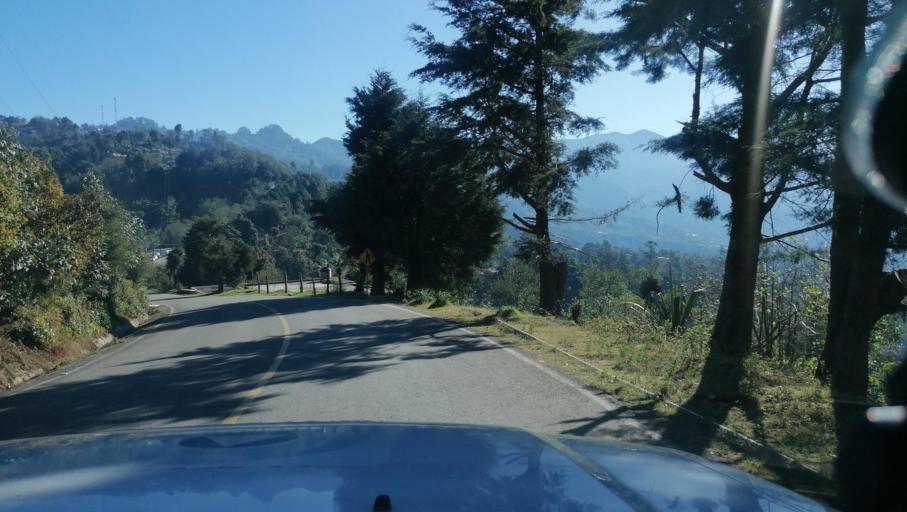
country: MX
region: Chiapas
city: Motozintla de Mendoza
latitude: 15.2527
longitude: -92.2197
